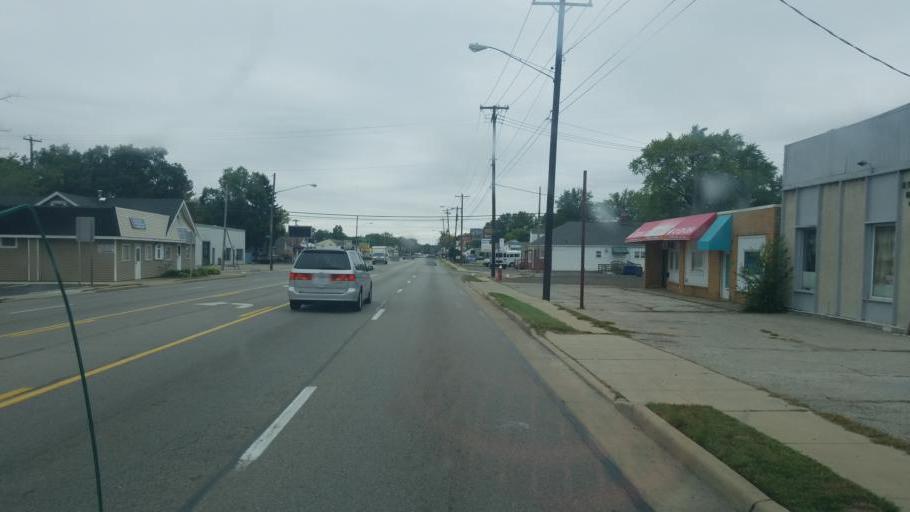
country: US
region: Ohio
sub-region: Lucas County
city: Ottawa Hills
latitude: 41.6579
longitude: -83.6675
